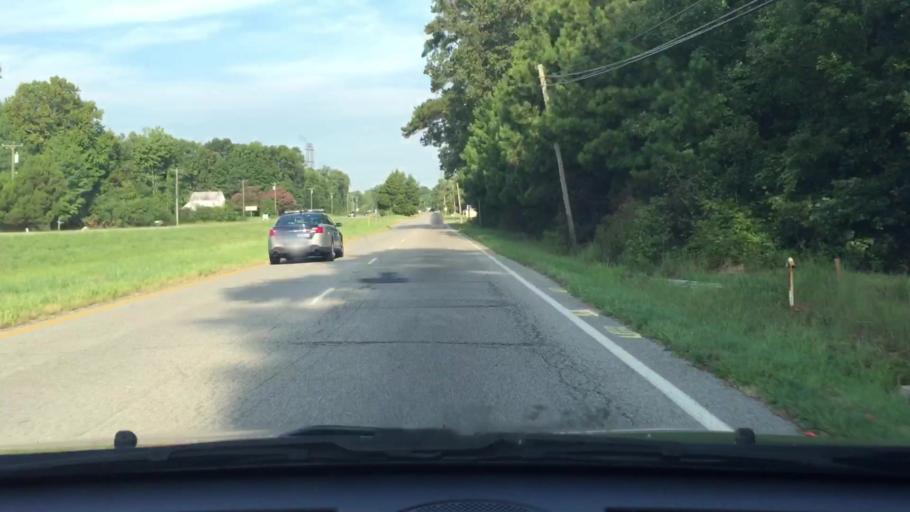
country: US
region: Virginia
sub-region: Isle of Wight County
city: Carrollton
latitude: 36.9412
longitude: -76.5442
